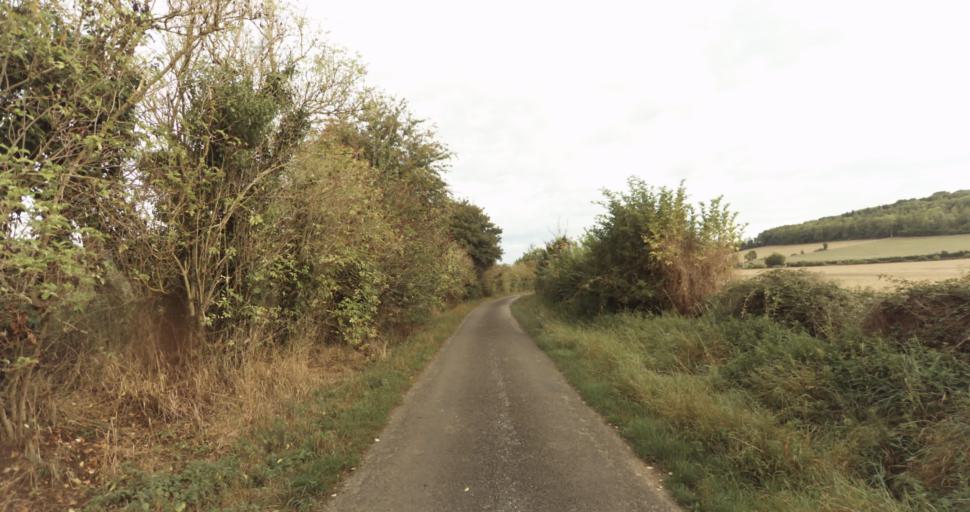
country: FR
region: Lower Normandy
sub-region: Departement de l'Orne
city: Vimoutiers
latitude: 48.9429
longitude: 0.2744
